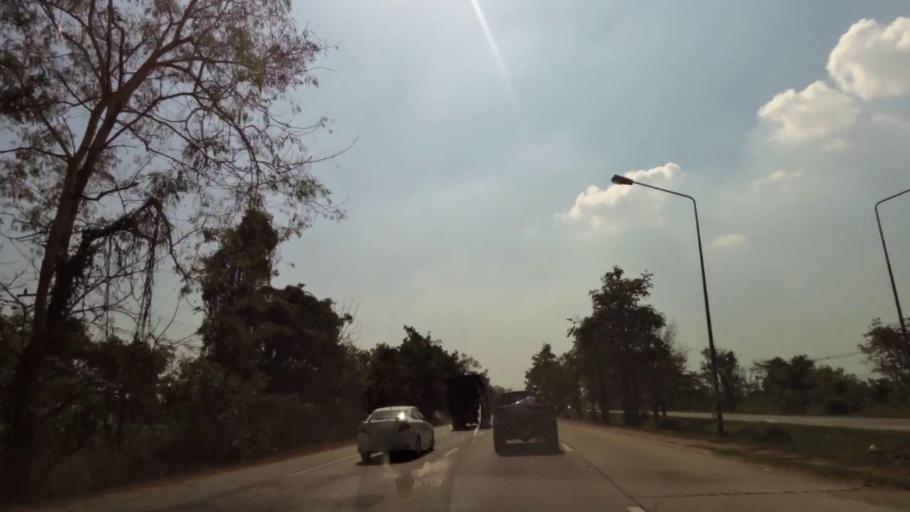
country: TH
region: Phichit
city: Wachira Barami
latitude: 16.5465
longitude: 100.1459
